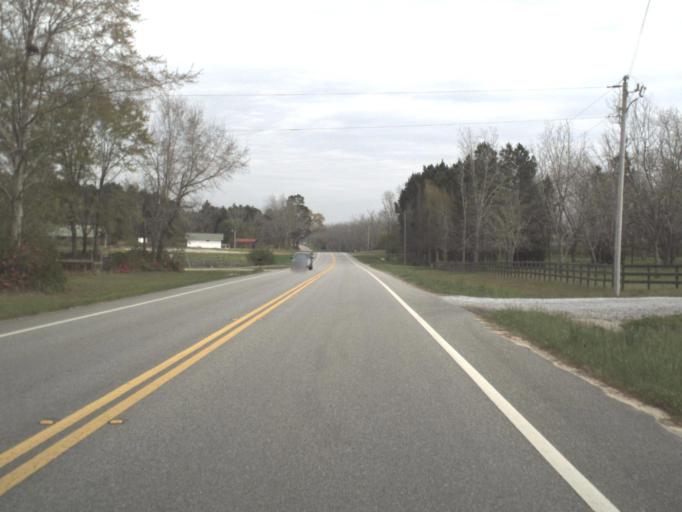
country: US
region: Florida
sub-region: Holmes County
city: Bonifay
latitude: 30.9118
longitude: -85.6500
